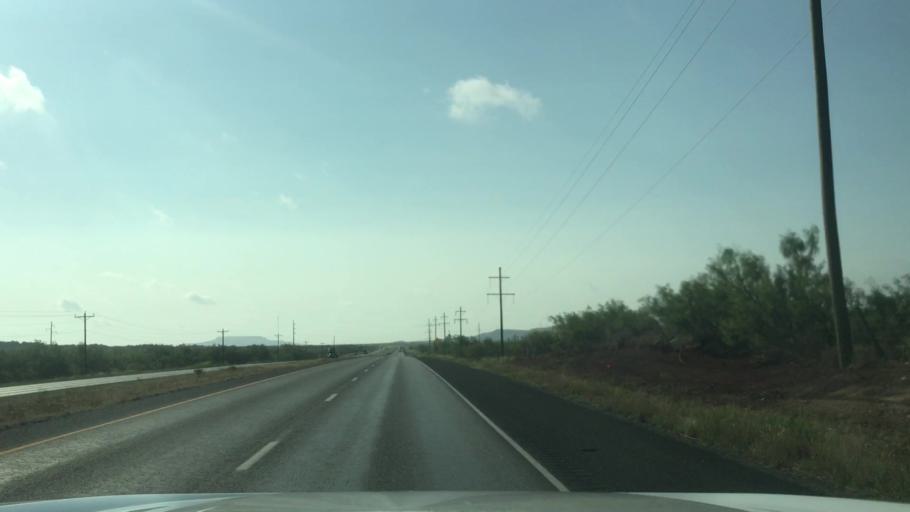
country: US
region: Texas
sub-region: Garza County
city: Post
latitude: 32.9984
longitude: -101.1557
